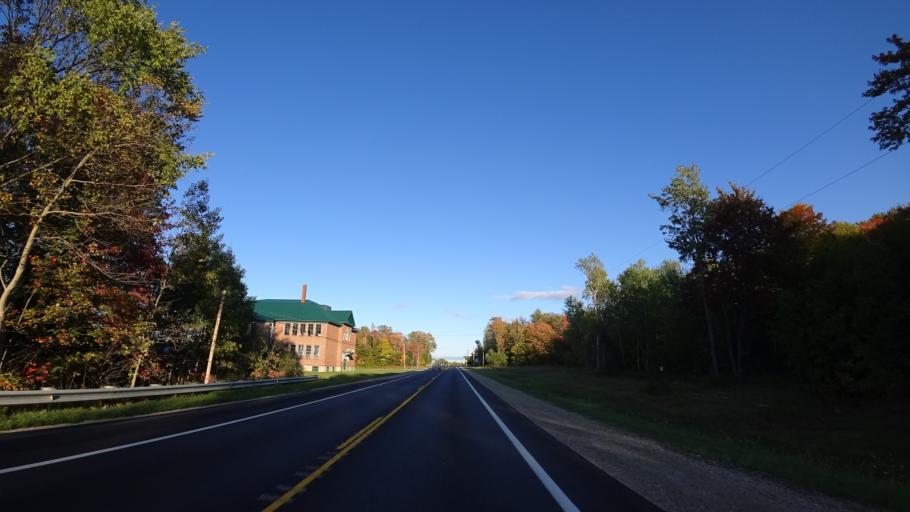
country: US
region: Michigan
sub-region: Luce County
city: Newberry
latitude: 46.3390
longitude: -85.6928
